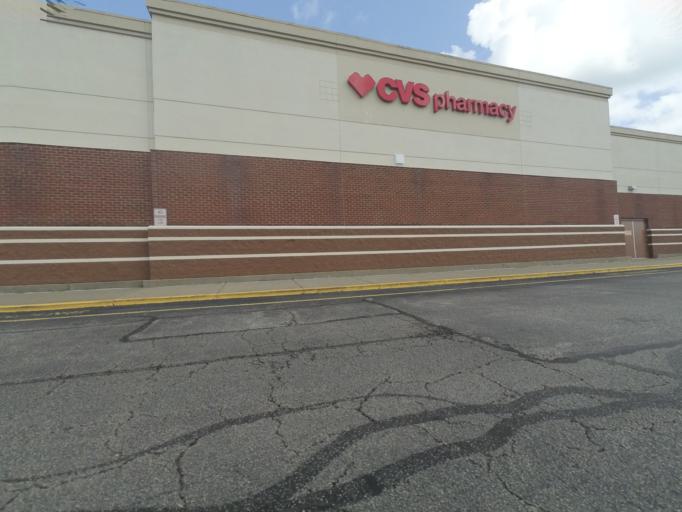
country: US
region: West Virginia
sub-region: Cabell County
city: Barboursville
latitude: 38.4198
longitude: -82.2853
